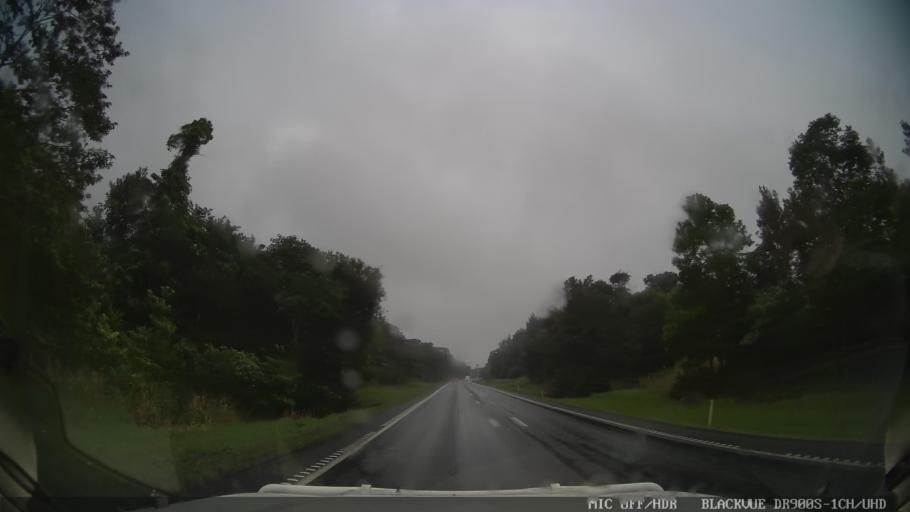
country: AU
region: Queensland
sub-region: Cassowary Coast
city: Innisfail
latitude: -17.8561
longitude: 145.9867
